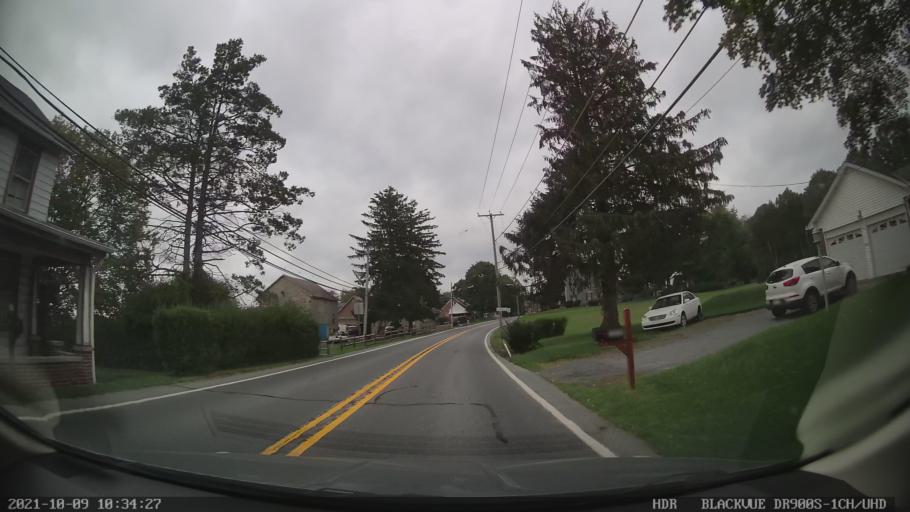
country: US
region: Pennsylvania
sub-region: Berks County
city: Topton
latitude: 40.5009
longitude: -75.6573
